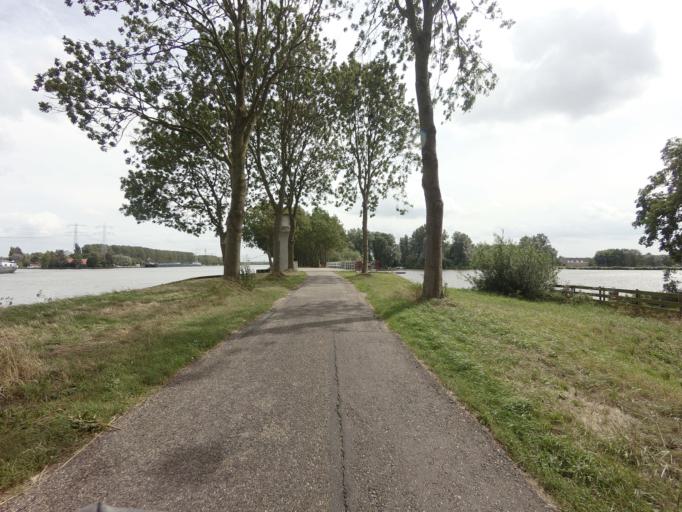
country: NL
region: North Holland
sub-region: Gemeente Diemen
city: Diemen
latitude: 52.3420
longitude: 4.9974
